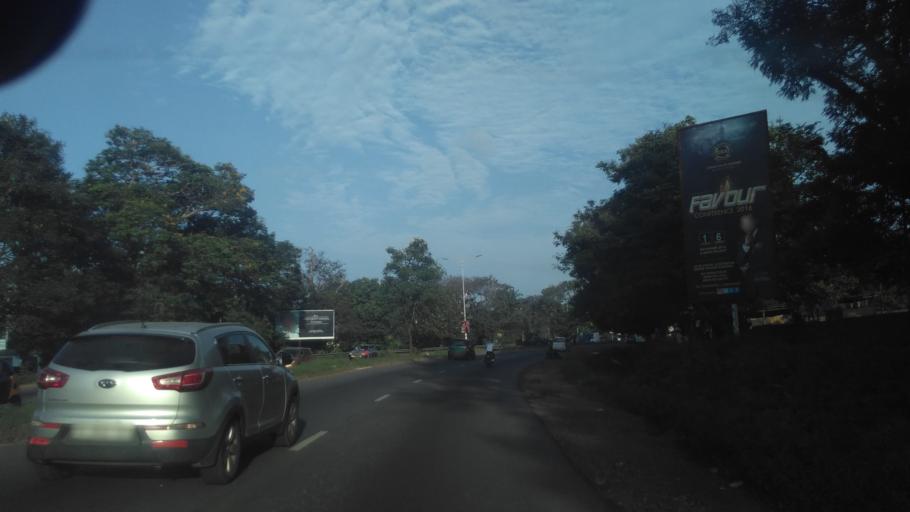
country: GH
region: Greater Accra
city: Accra
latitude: 5.5744
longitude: -0.1954
